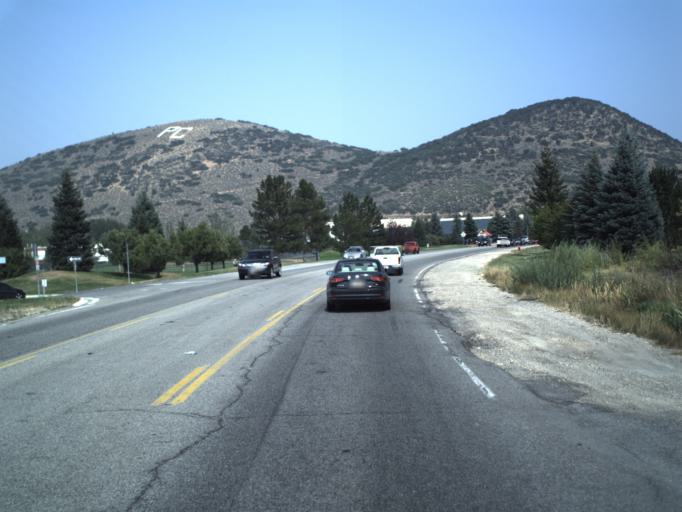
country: US
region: Utah
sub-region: Summit County
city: Park City
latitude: 40.6670
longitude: -111.4952
